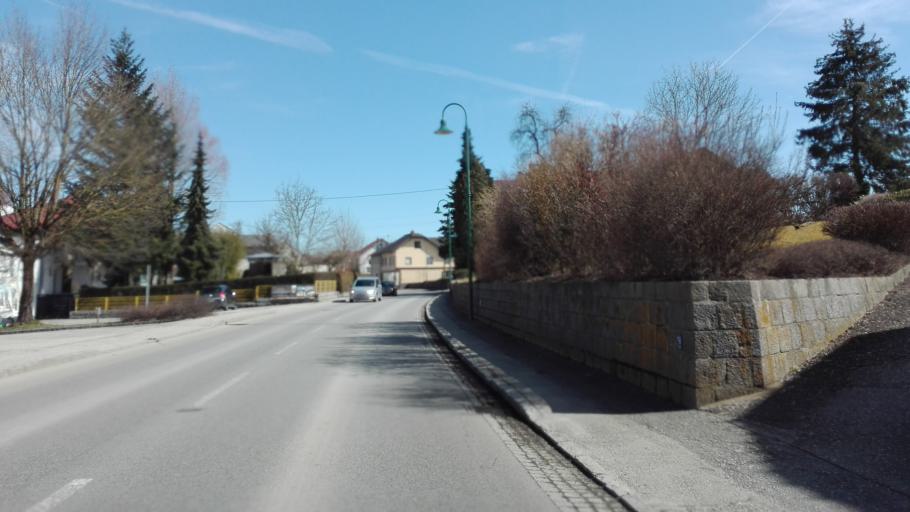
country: AT
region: Upper Austria
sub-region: Politischer Bezirk Scharding
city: Sankt Marienkirchen bei Schaerding
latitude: 48.3520
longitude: 13.6418
